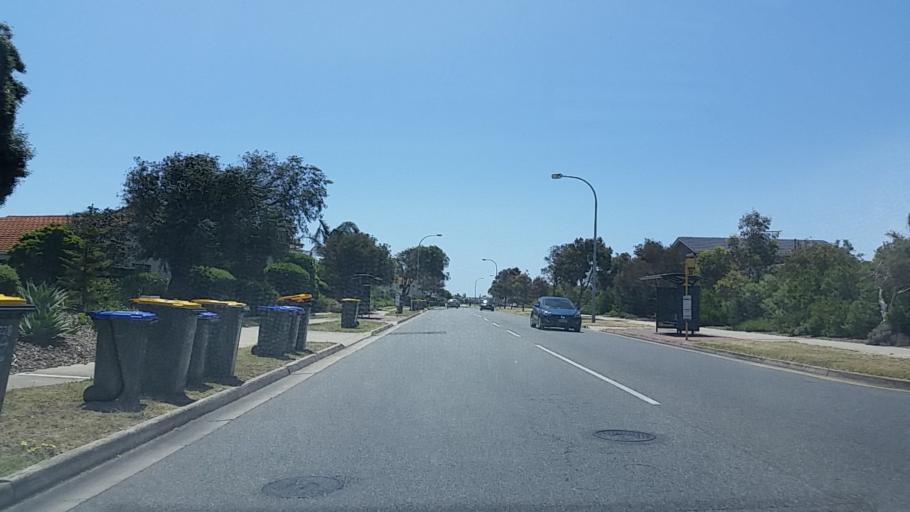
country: AU
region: South Australia
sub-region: Charles Sturt
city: Grange
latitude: -34.8921
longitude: 138.4919
